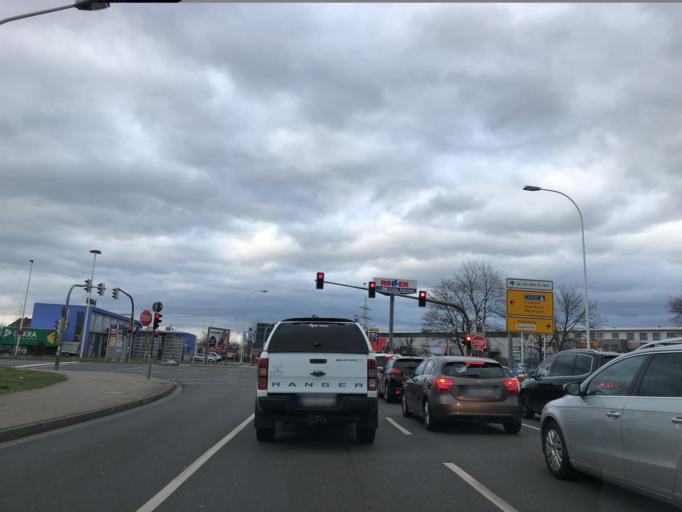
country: DE
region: Hesse
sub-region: Regierungsbezirk Darmstadt
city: Darmstadt
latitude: 49.8879
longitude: 8.6453
